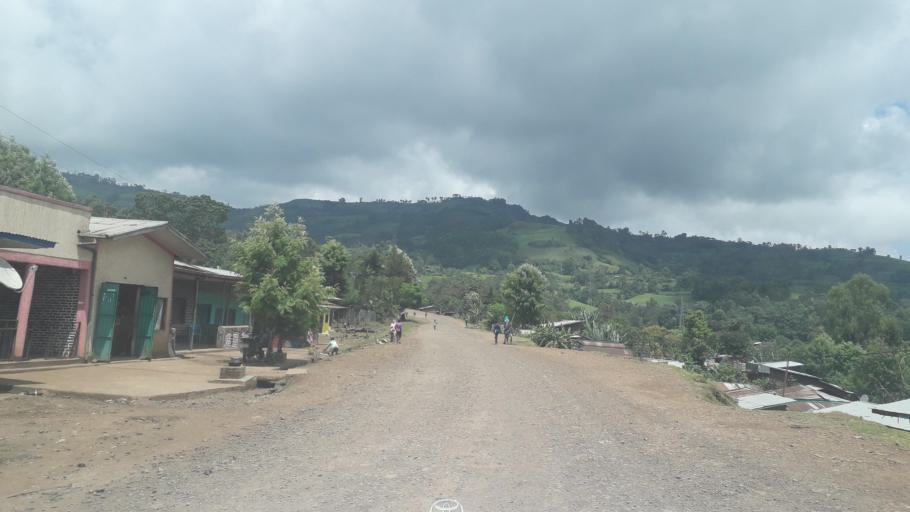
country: ET
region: Oromiya
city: Jima
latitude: 7.4217
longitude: 36.8729
